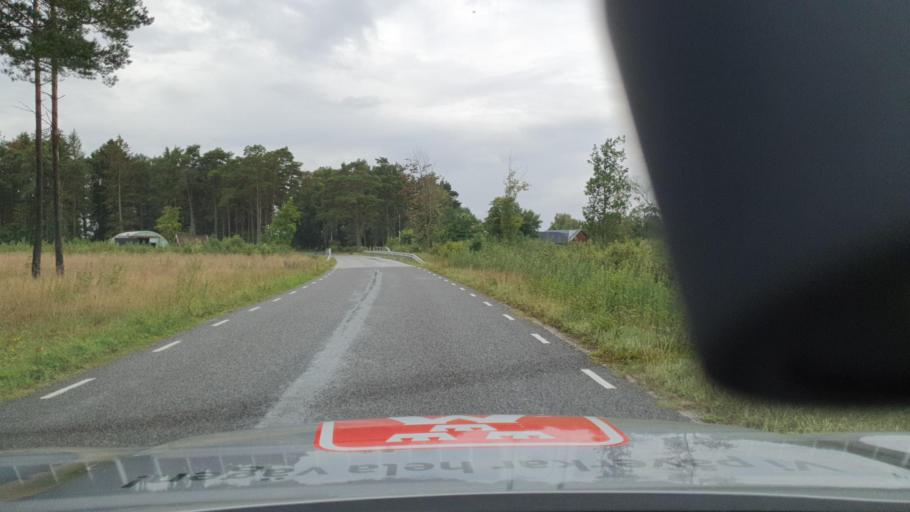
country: SE
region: Gotland
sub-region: Gotland
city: Visby
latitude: 57.5738
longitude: 18.4857
